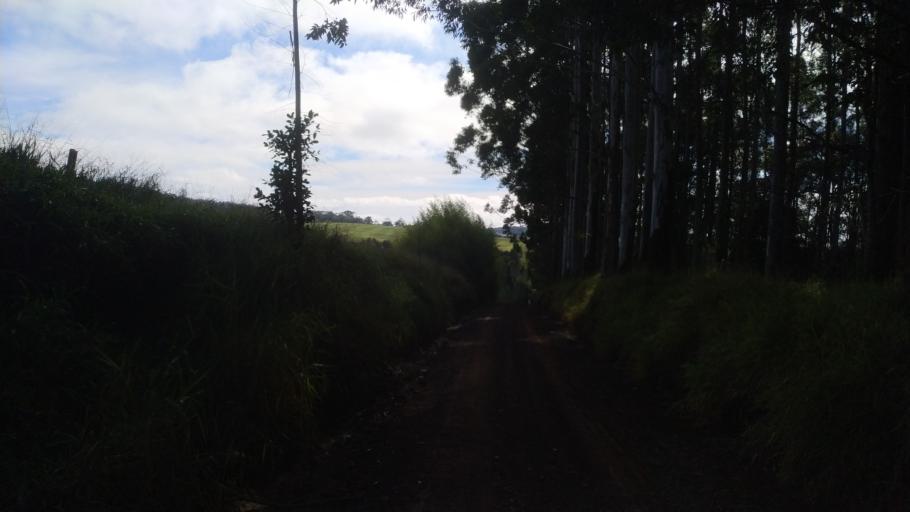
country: BR
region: Santa Catarina
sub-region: Chapeco
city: Chapeco
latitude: -27.1582
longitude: -52.5966
